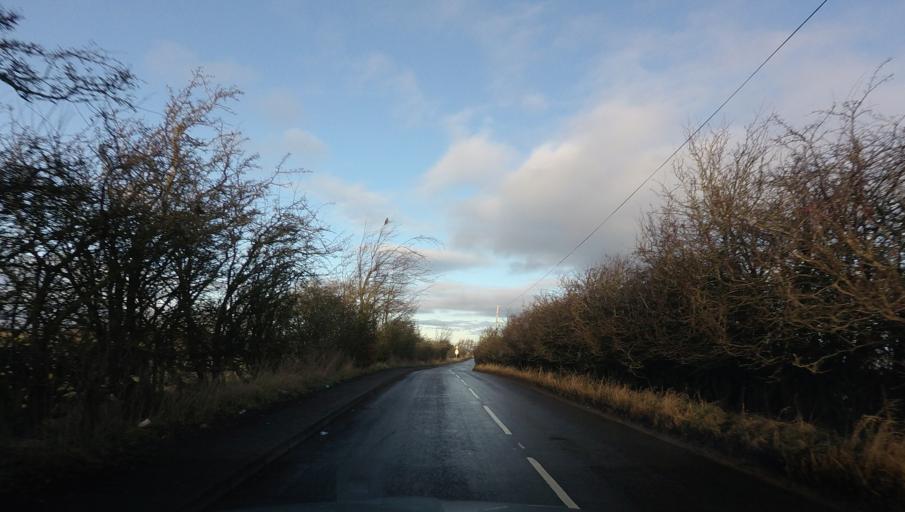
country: GB
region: Scotland
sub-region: West Lothian
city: East Calder
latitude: 55.8945
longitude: -3.4422
